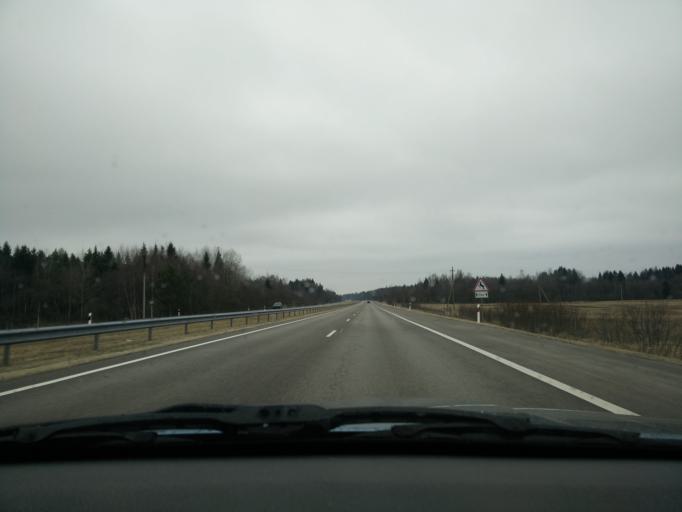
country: LT
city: Silale
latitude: 55.6034
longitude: 22.1006
